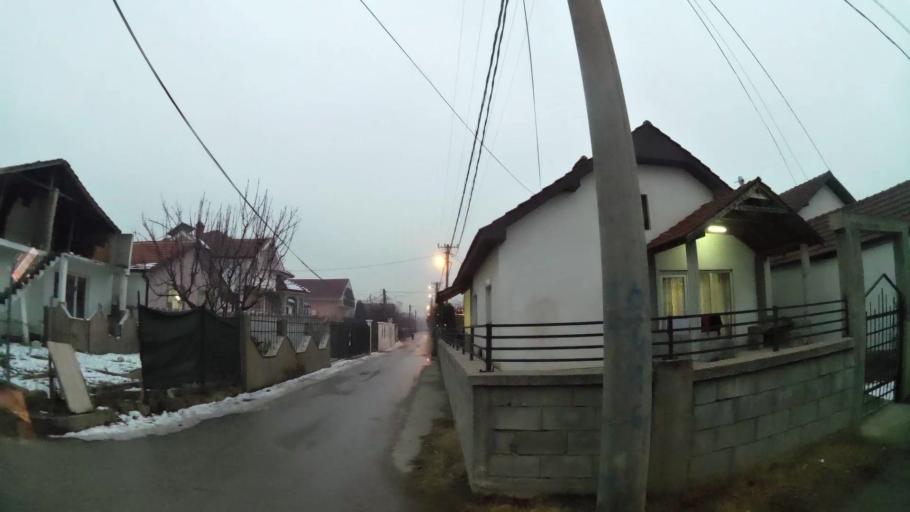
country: MK
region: Kisela Voda
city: Kisela Voda
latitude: 41.9748
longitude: 21.4937
